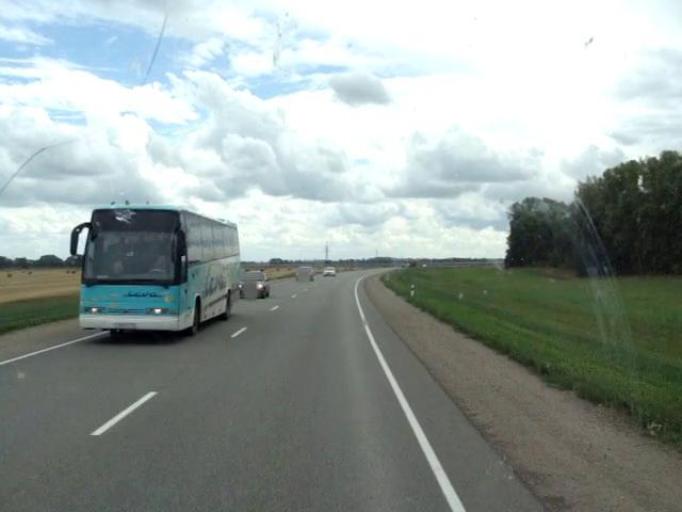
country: RU
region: Altai Krai
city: Shubenka
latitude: 52.6826
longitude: 85.0459
